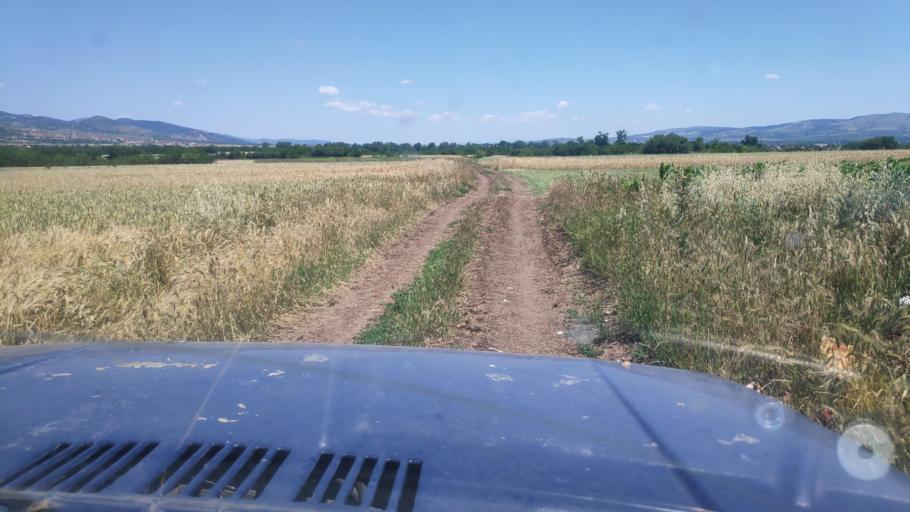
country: MK
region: Kumanovo
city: Bedinje
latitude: 42.1656
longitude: 21.6841
